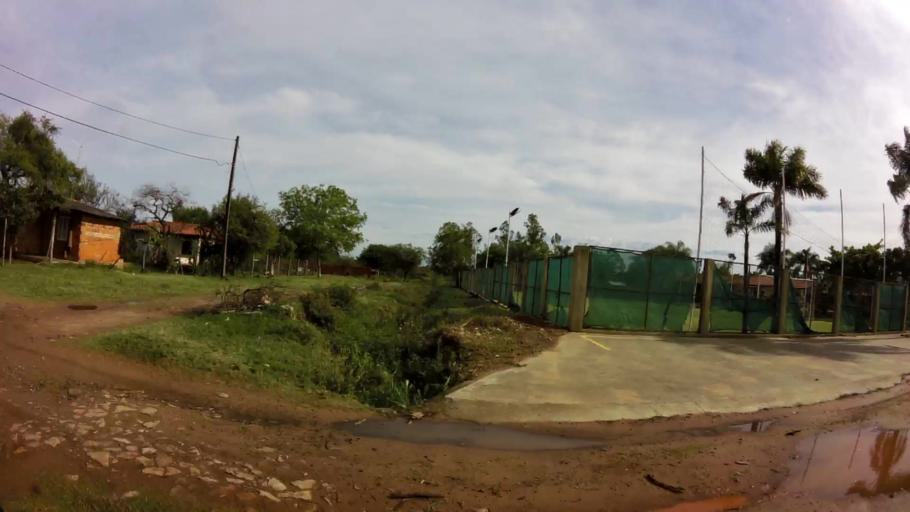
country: PY
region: Central
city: Limpio
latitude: -25.1671
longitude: -57.4865
